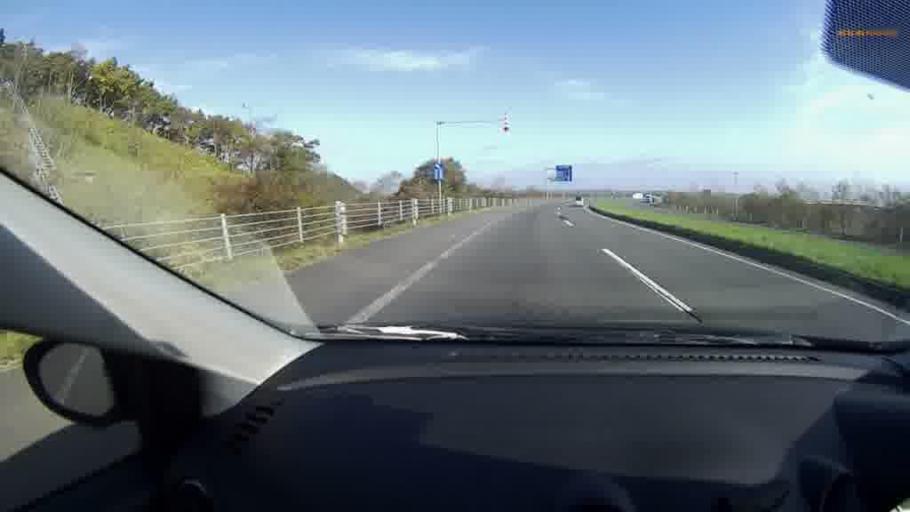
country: JP
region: Hokkaido
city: Kushiro
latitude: 43.0177
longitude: 144.2566
